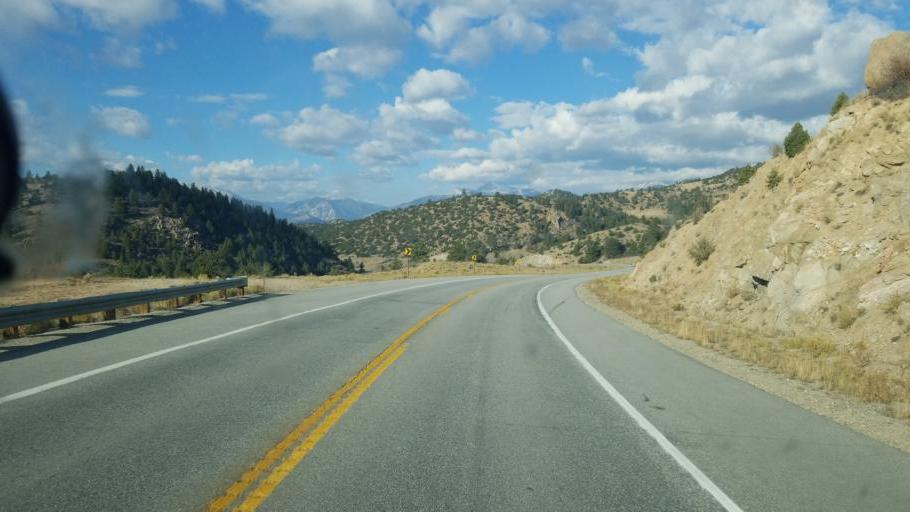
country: US
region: Colorado
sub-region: Chaffee County
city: Buena Vista
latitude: 38.8409
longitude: -106.0038
